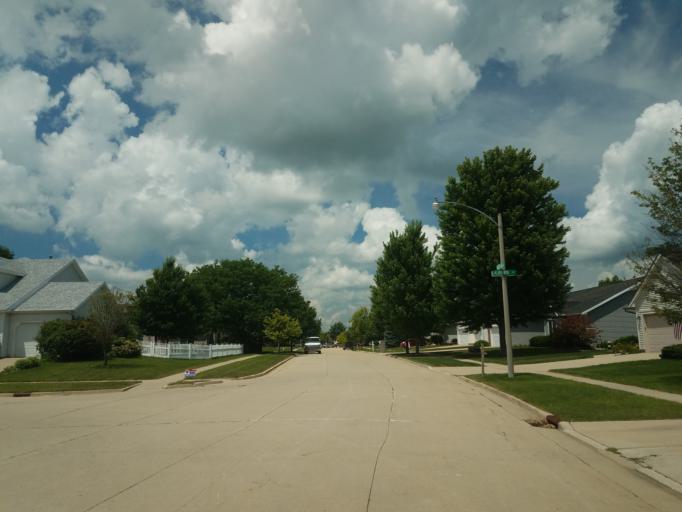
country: US
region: Illinois
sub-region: McLean County
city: Normal
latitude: 40.4974
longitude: -88.9192
